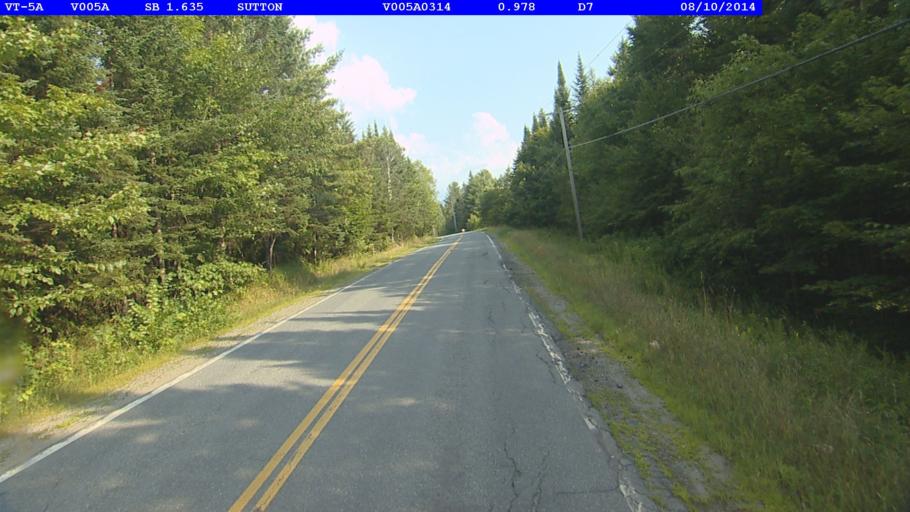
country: US
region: Vermont
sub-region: Caledonia County
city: Lyndonville
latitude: 44.6616
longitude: -71.9912
